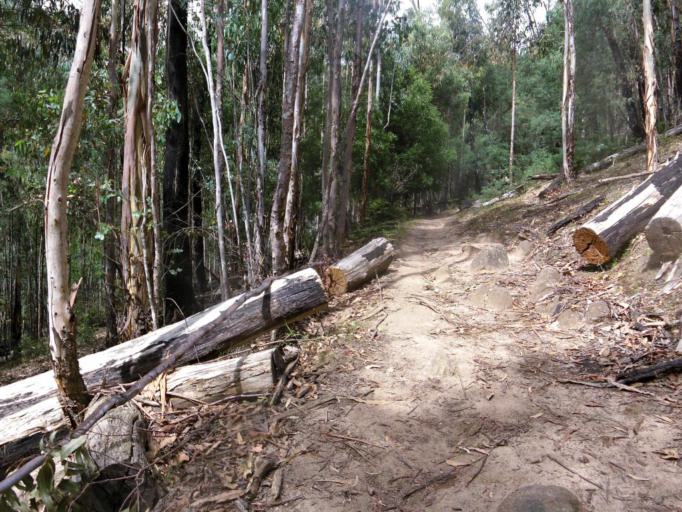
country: AU
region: Victoria
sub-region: Yarra Ranges
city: Healesville
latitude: -37.4042
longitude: 145.5678
